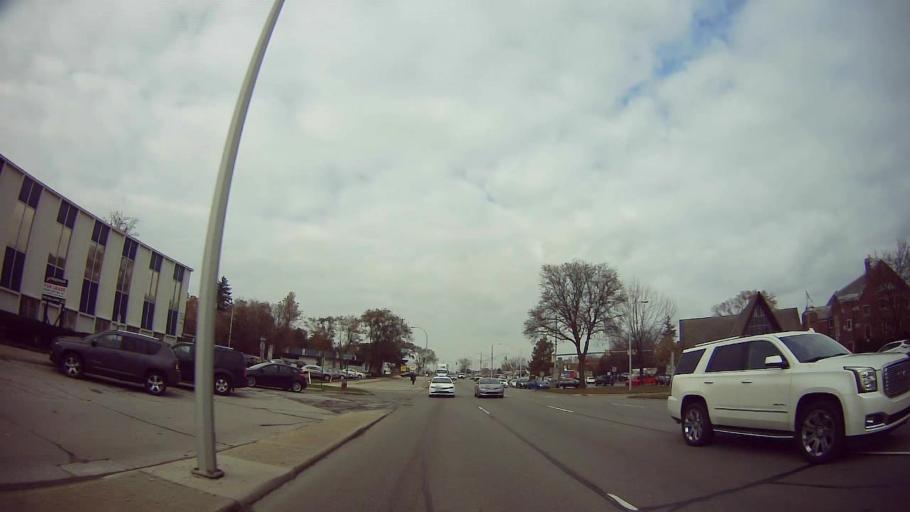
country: US
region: Michigan
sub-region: Oakland County
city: Huntington Woods
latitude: 42.4881
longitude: -83.1578
